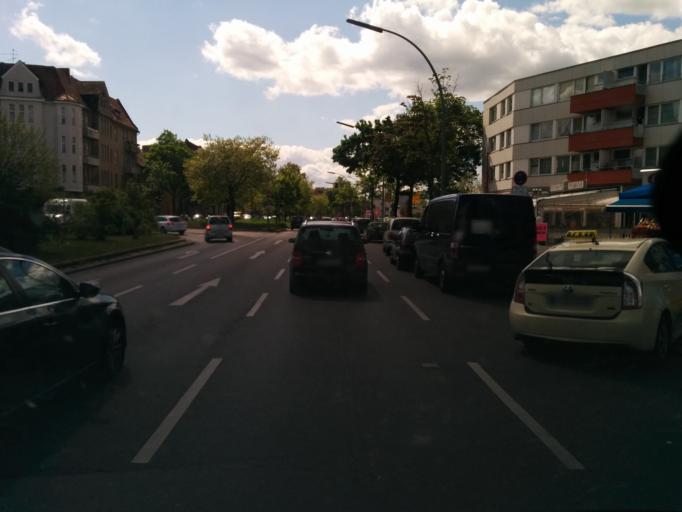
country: DE
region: Berlin
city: Wilhelmstadt
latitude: 52.5284
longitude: 13.1952
